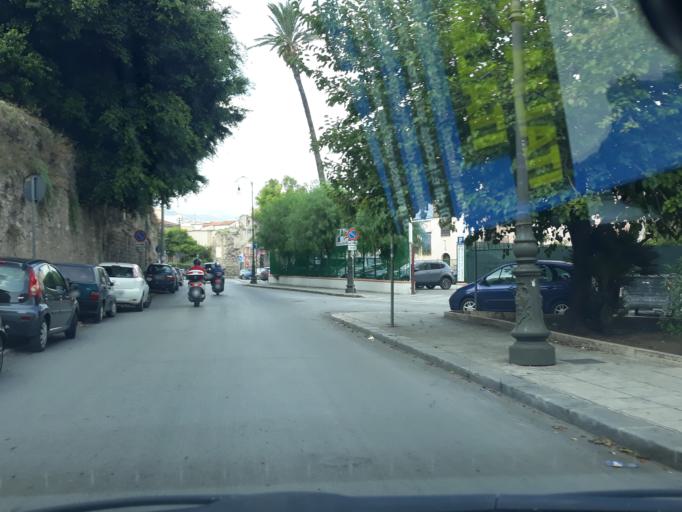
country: IT
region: Sicily
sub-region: Palermo
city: Palermo
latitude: 38.1088
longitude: 13.3571
